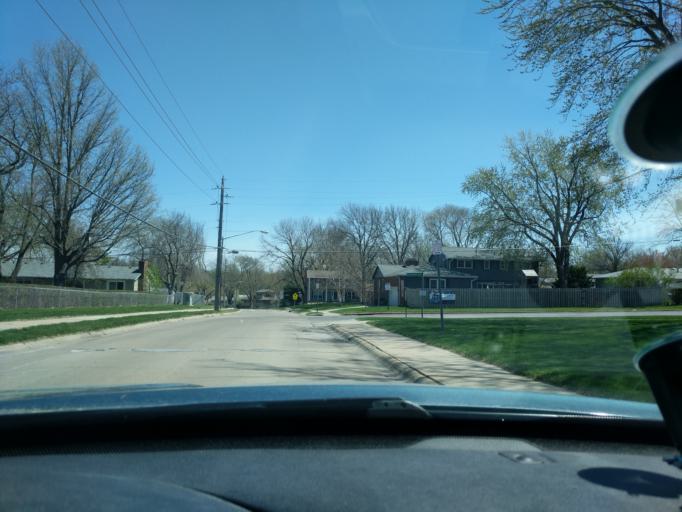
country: US
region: Nebraska
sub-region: Douglas County
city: Ralston
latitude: 41.2266
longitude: -96.0987
